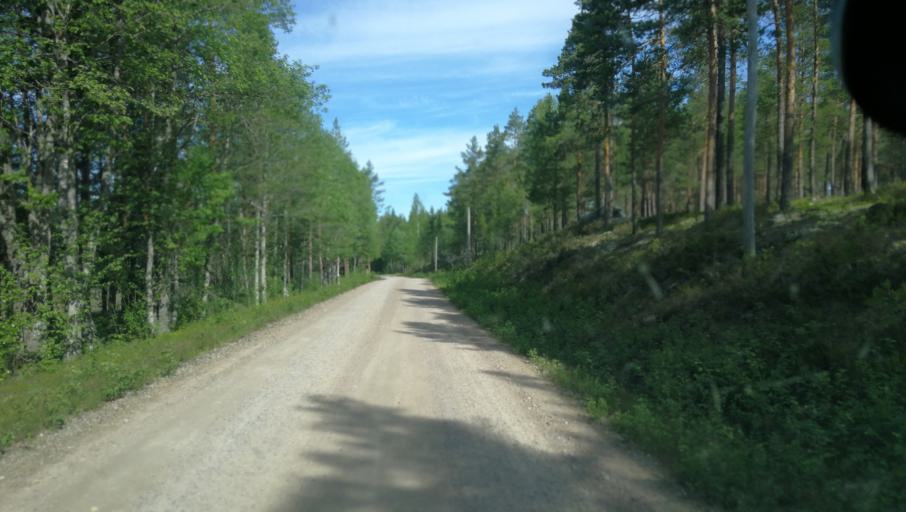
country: SE
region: Dalarna
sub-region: Vansbro Kommun
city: Vansbro
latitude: 60.8380
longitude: 14.1498
